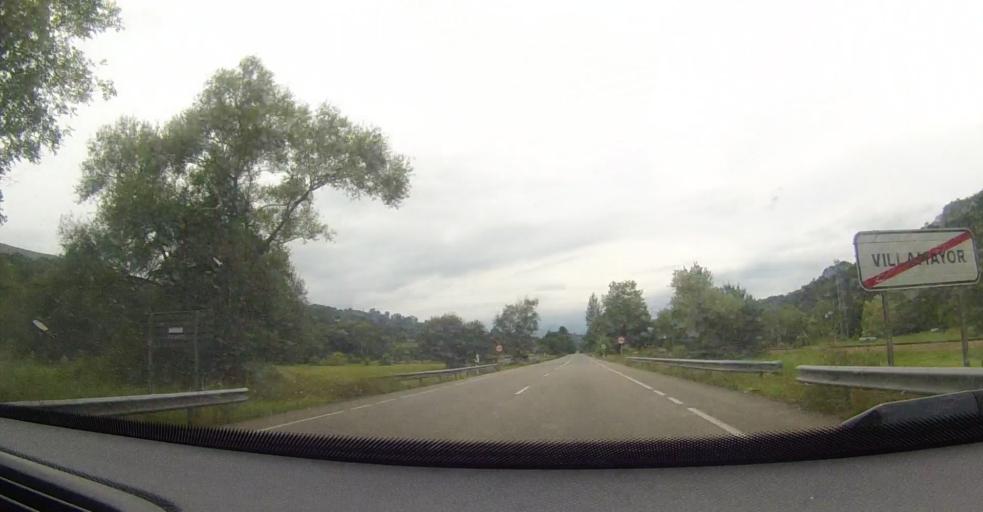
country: ES
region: Asturias
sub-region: Province of Asturias
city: Pilona
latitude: 43.3565
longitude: -5.3125
